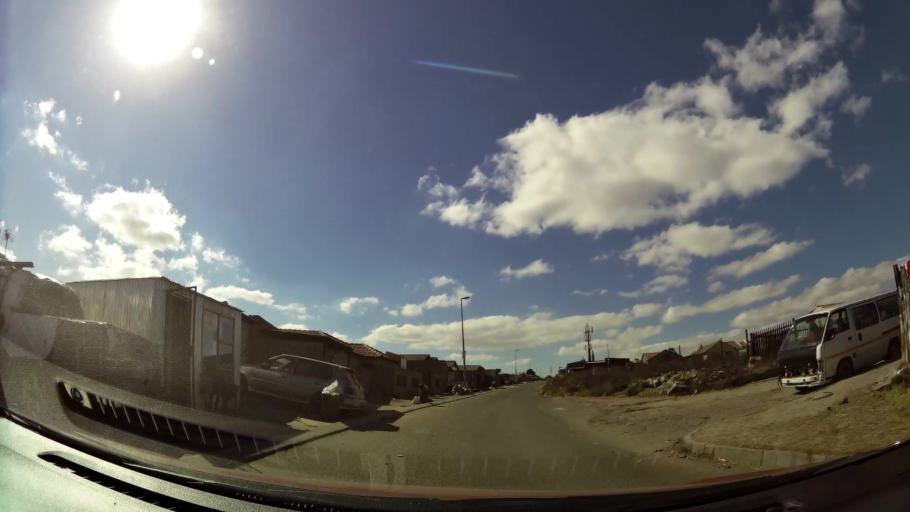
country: ZA
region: Gauteng
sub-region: City of Johannesburg Metropolitan Municipality
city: Midrand
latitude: -26.0325
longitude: 28.1645
